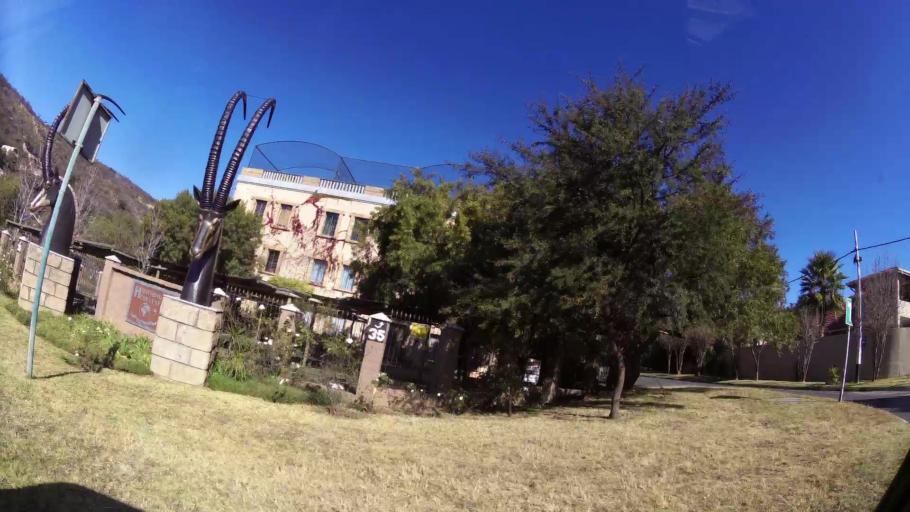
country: ZA
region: Gauteng
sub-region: City of Johannesburg Metropolitan Municipality
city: Johannesburg
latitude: -26.2813
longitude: 28.0077
